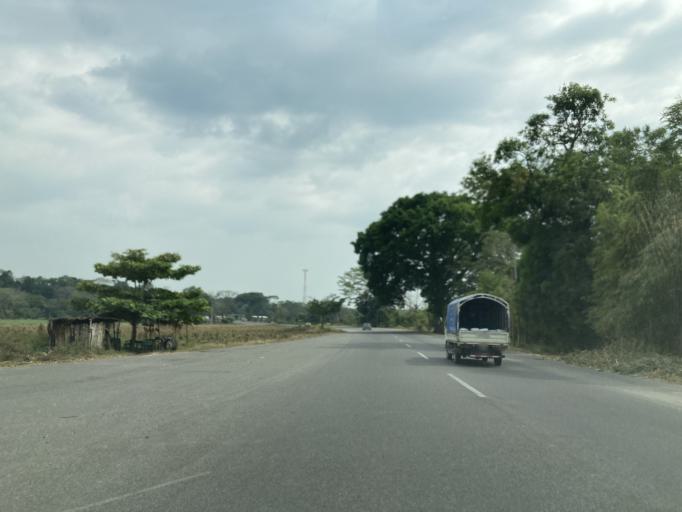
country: GT
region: Suchitepeque
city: Rio Bravo
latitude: 14.4162
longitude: -91.3620
